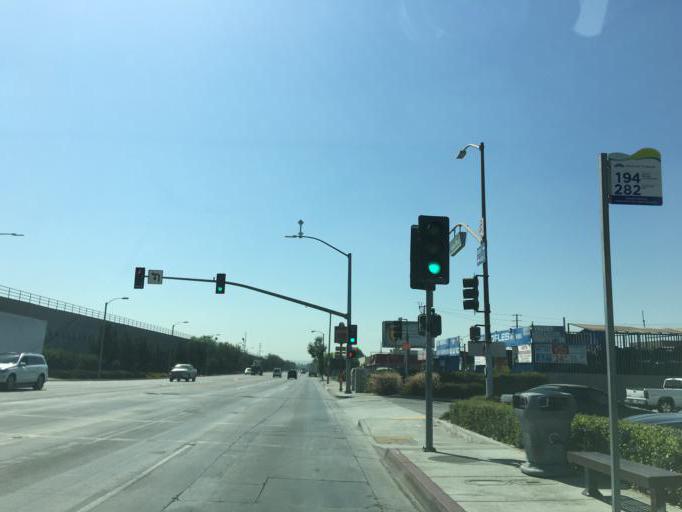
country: US
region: California
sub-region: Los Angeles County
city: Avocado Heights
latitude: 34.0381
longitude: -117.9797
